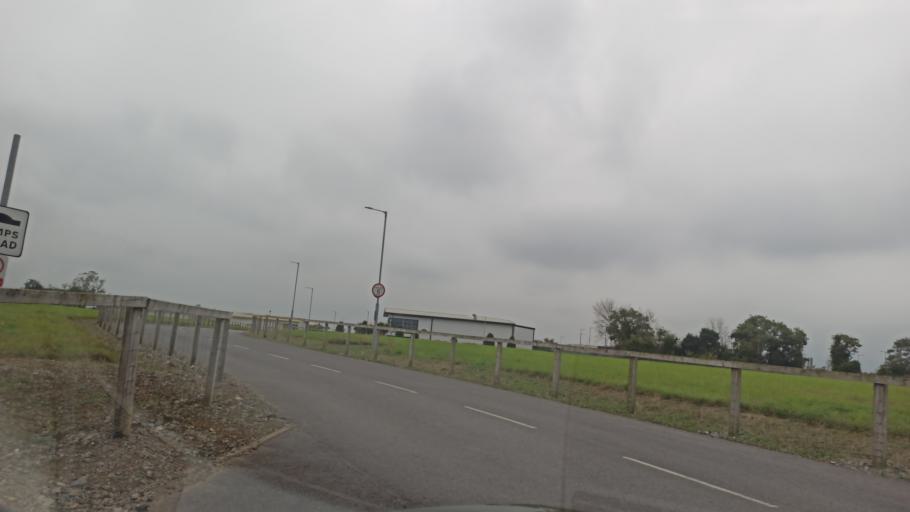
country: IE
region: Munster
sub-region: South Tipperary
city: Cluain Meala
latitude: 52.3744
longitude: -7.7279
